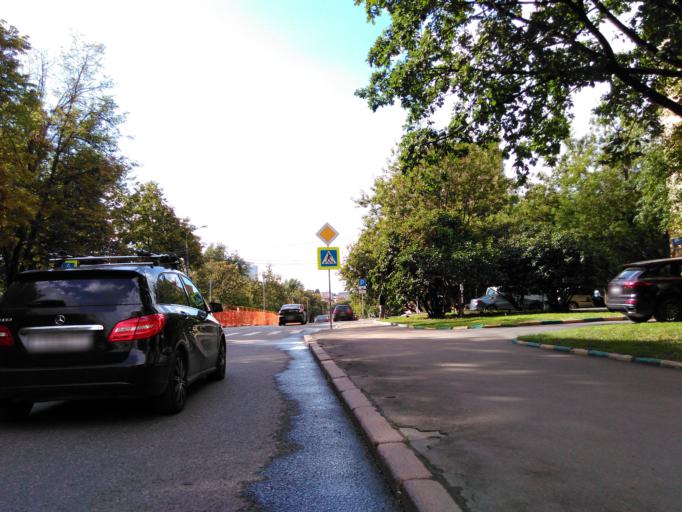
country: RU
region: Moscow
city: Luzhniki
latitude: 55.7281
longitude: 37.5598
